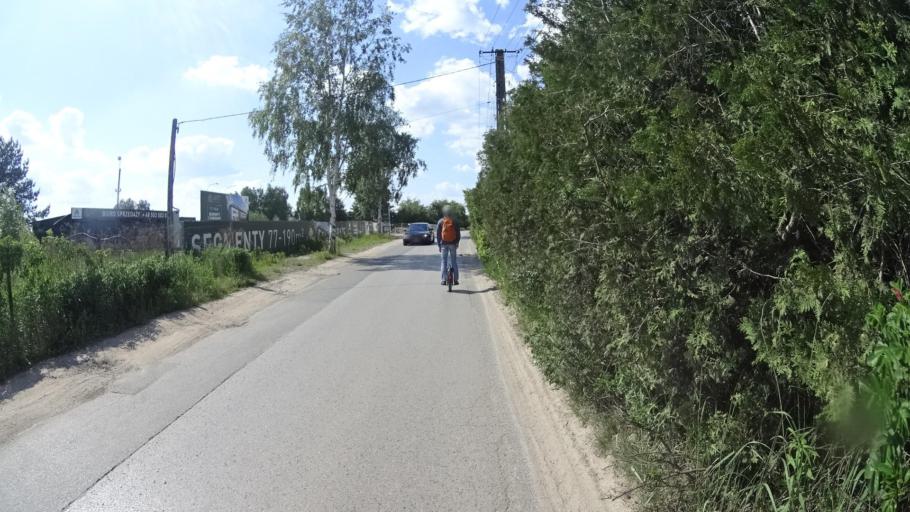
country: PL
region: Masovian Voivodeship
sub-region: Powiat piaseczynski
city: Jozefoslaw
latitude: 52.1005
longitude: 21.0659
